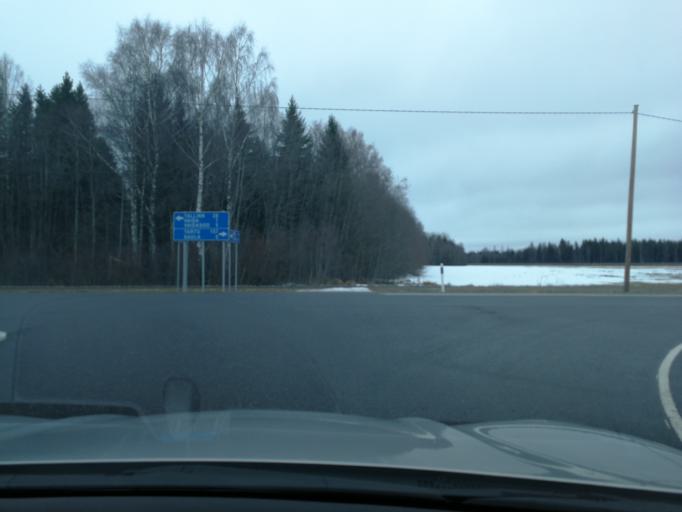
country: EE
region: Harju
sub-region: Rae vald
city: Vaida
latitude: 59.2360
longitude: 25.0225
